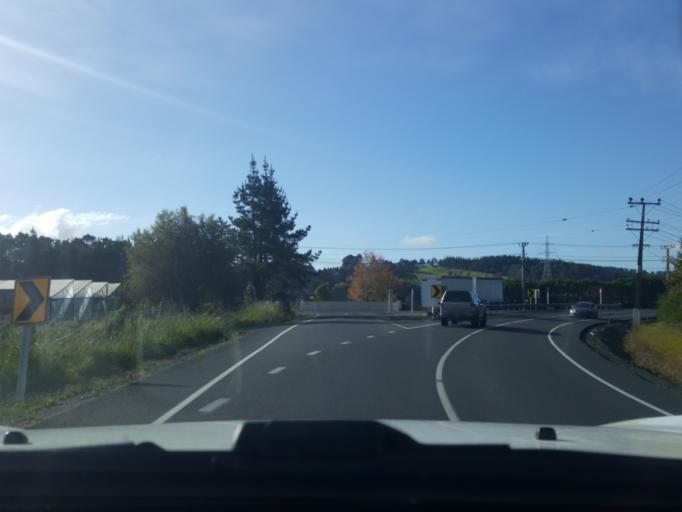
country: NZ
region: Auckland
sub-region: Auckland
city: Muriwai Beach
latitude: -36.7631
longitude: 174.5770
